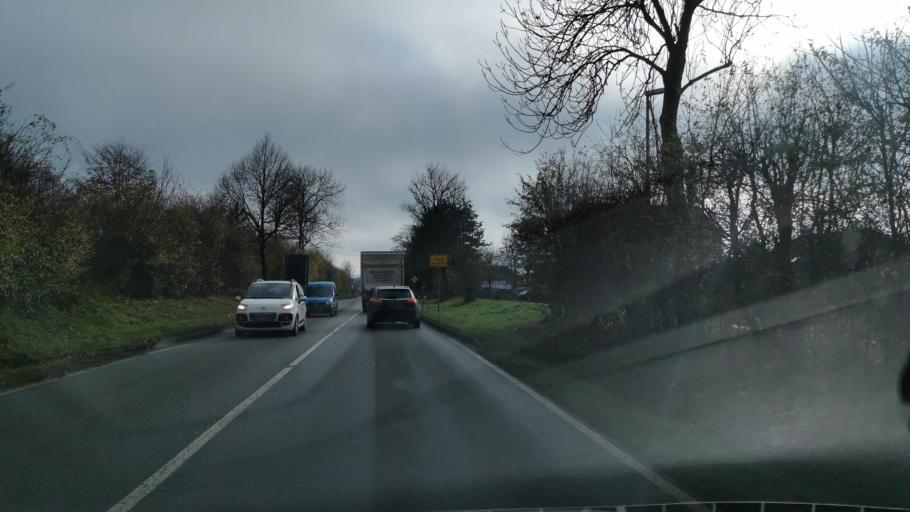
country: DE
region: Rheinland-Pfalz
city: Faid
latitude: 50.1486
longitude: 7.1186
